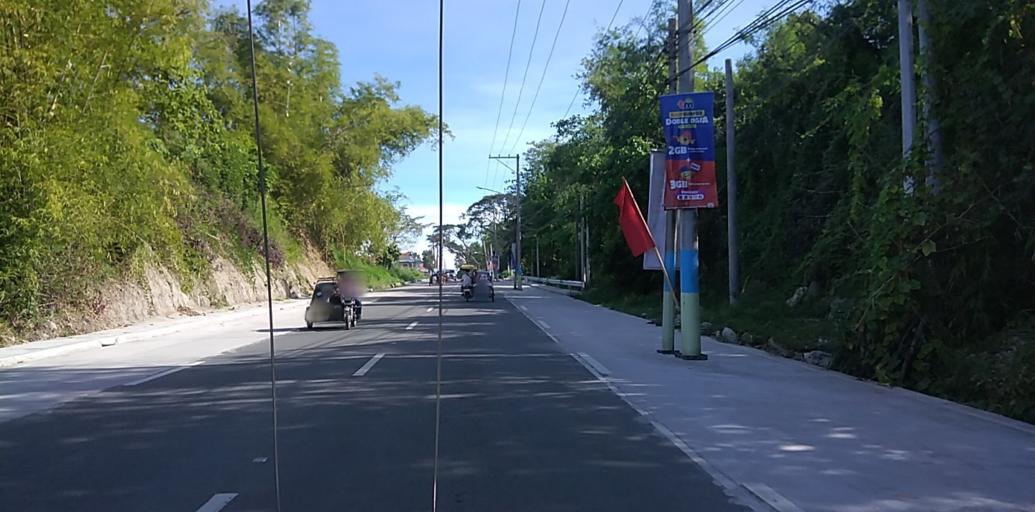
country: PH
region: Central Luzon
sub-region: Province of Pampanga
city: Porac
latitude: 15.0779
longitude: 120.5451
